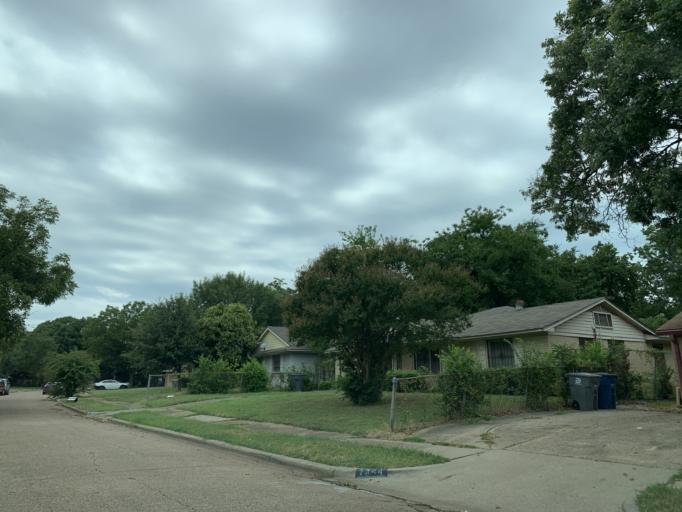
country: US
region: Texas
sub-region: Dallas County
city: DeSoto
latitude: 32.6582
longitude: -96.8253
